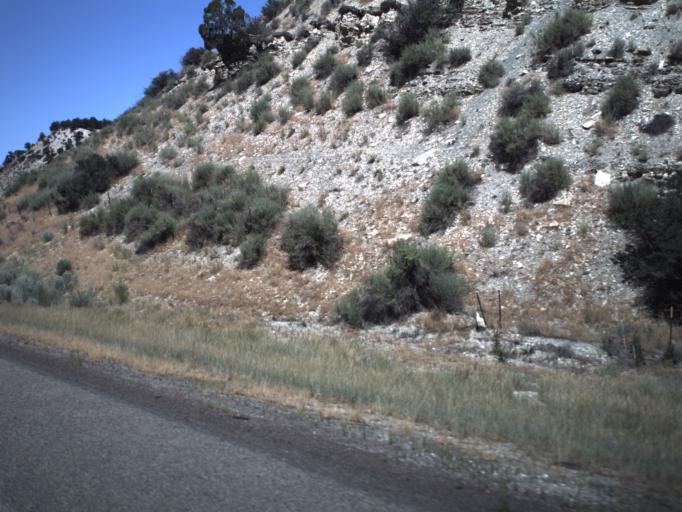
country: US
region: Utah
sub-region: Utah County
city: Mapleton
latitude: 39.9520
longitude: -111.2853
